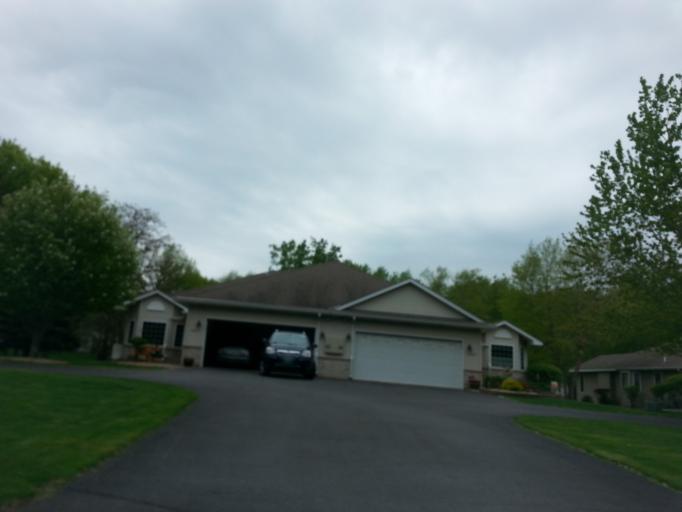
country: US
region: Minnesota
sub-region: Washington County
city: Oakdale
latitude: 44.9704
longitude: -92.9786
